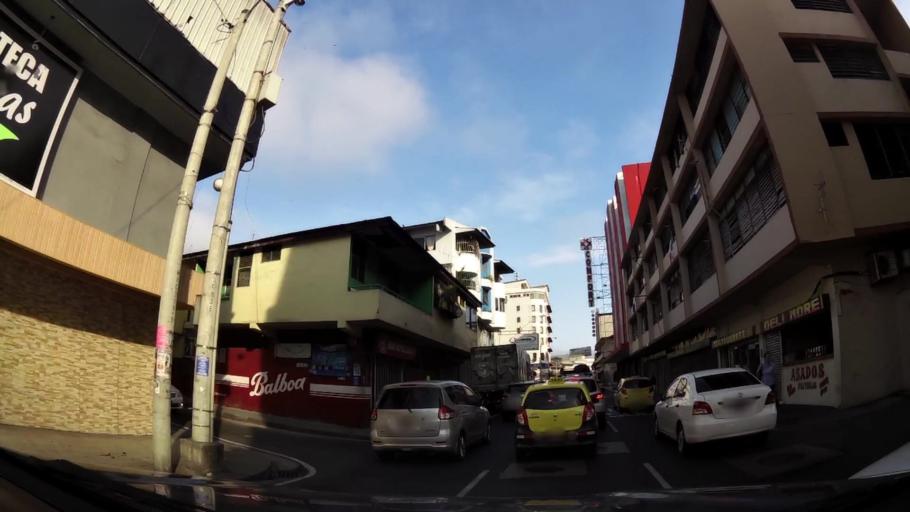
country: PA
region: Panama
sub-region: Distrito de Panama
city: Ancon
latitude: 8.9592
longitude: -79.5402
